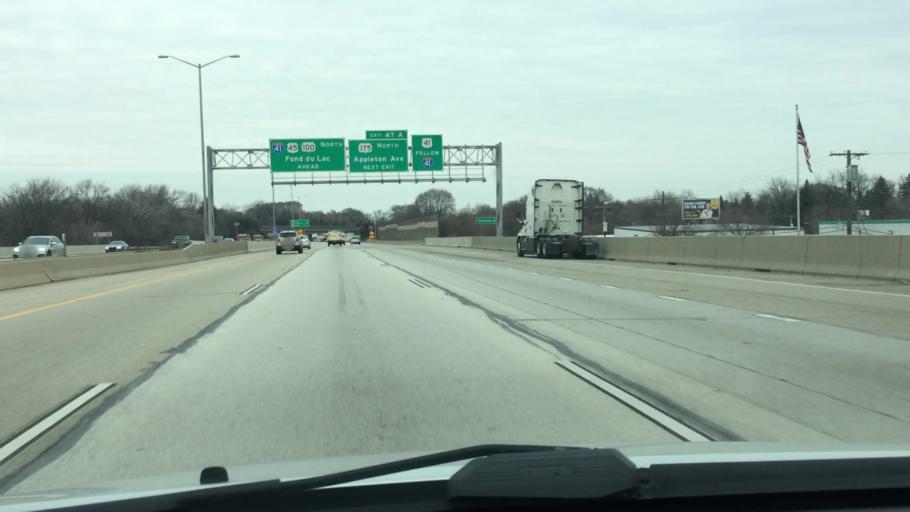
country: US
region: Wisconsin
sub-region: Waukesha County
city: Butler
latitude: 43.1218
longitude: -88.0569
